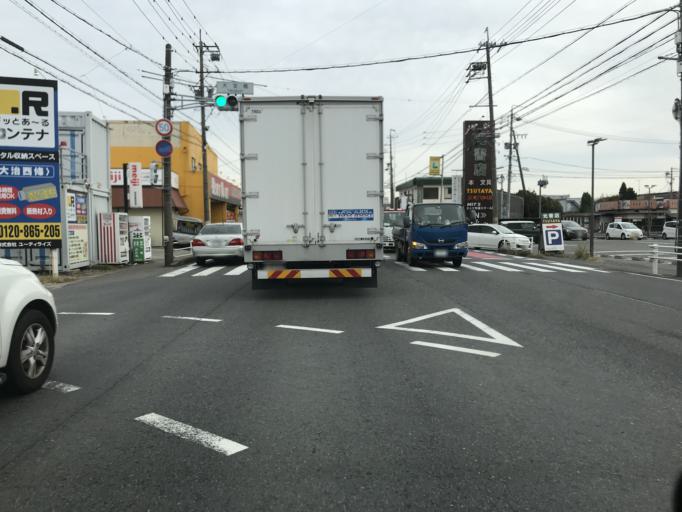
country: JP
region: Aichi
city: Kanie
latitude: 35.1841
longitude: 136.8105
